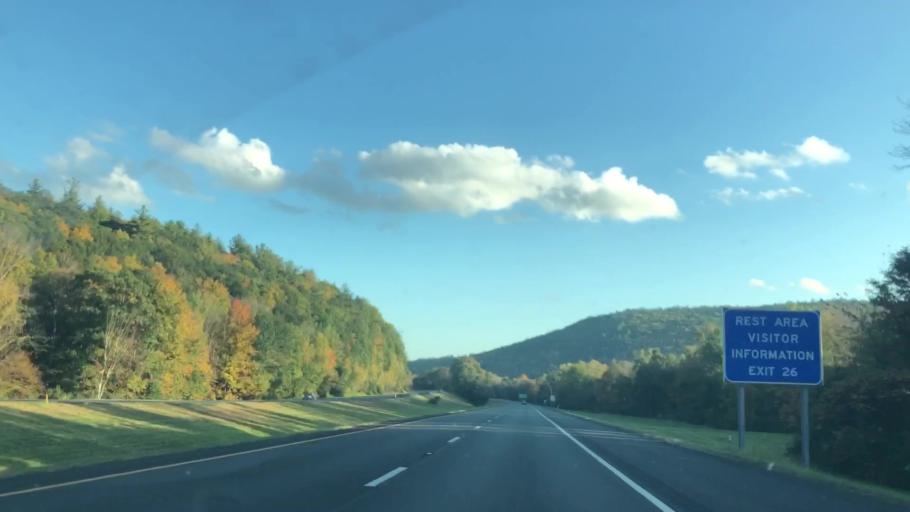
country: US
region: Massachusetts
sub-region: Franklin County
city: Bernardston
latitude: 42.7140
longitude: -72.5660
